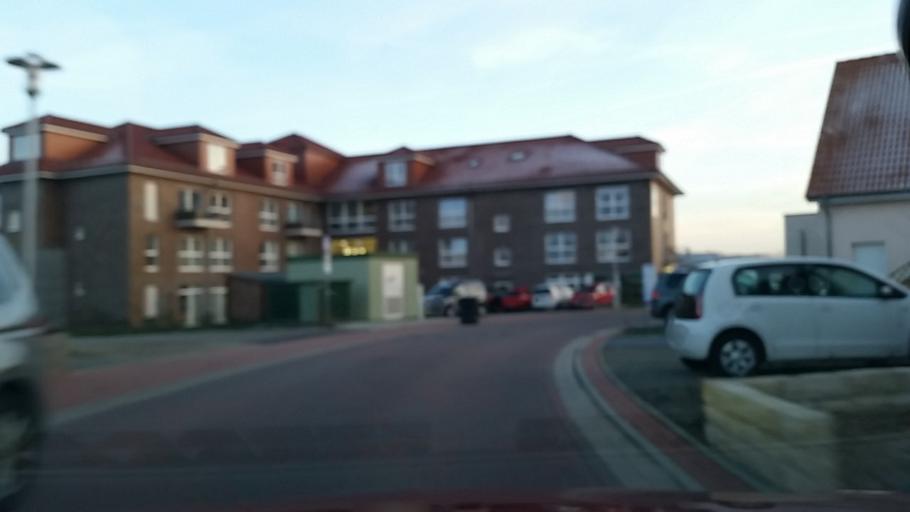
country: DE
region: Lower Saxony
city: Weyhausen
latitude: 52.4009
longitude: 10.7110
